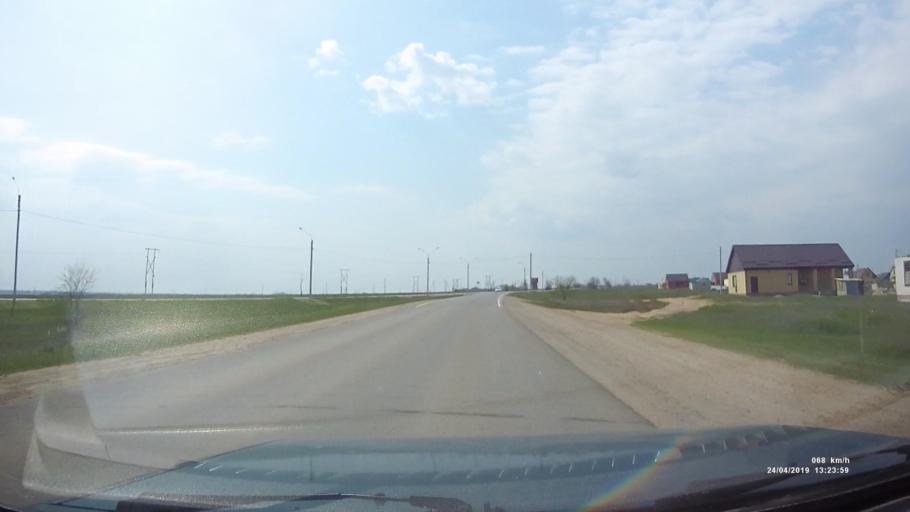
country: RU
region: Kalmykiya
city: Elista
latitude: 46.2833
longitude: 44.2612
